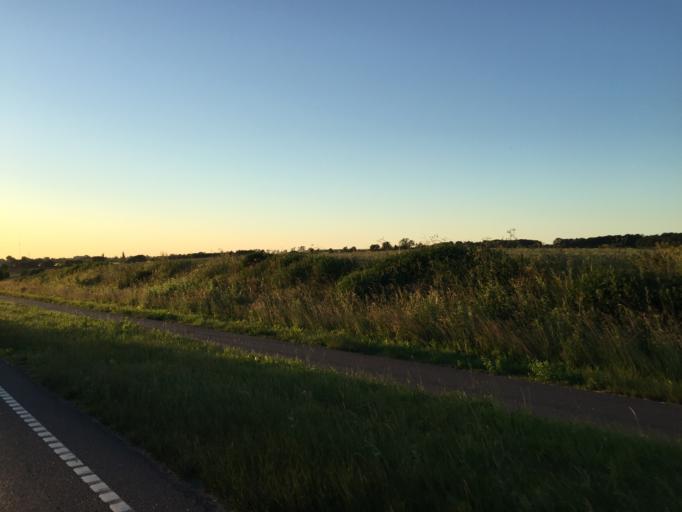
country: DK
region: South Denmark
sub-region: Nyborg Kommune
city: Nyborg
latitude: 55.3274
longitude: 10.7615
